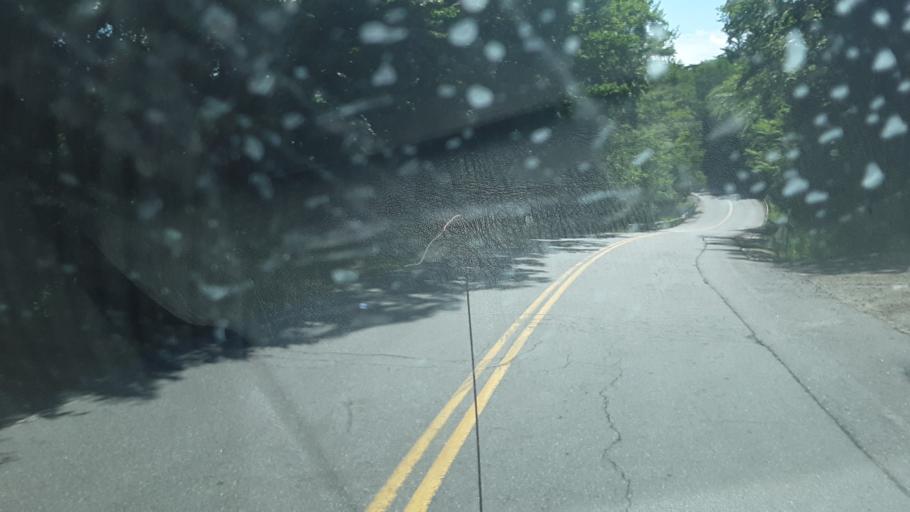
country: US
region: New Hampshire
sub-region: Grafton County
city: North Haverhill
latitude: 44.0979
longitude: -71.8589
